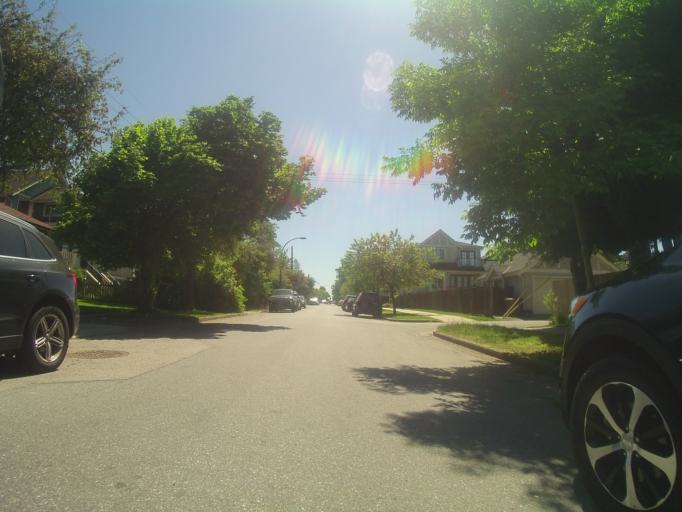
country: CA
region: British Columbia
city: Vancouver
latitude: 49.2507
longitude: -123.1049
